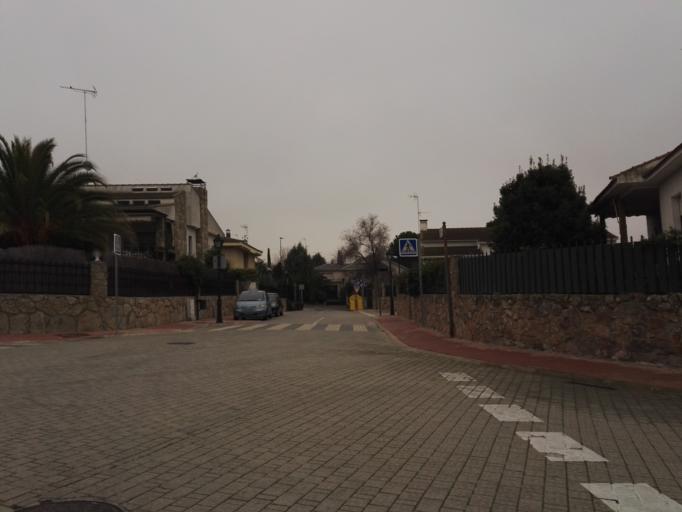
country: ES
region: Madrid
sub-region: Provincia de Madrid
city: Arroyomolinos
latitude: 40.2714
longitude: -3.9186
